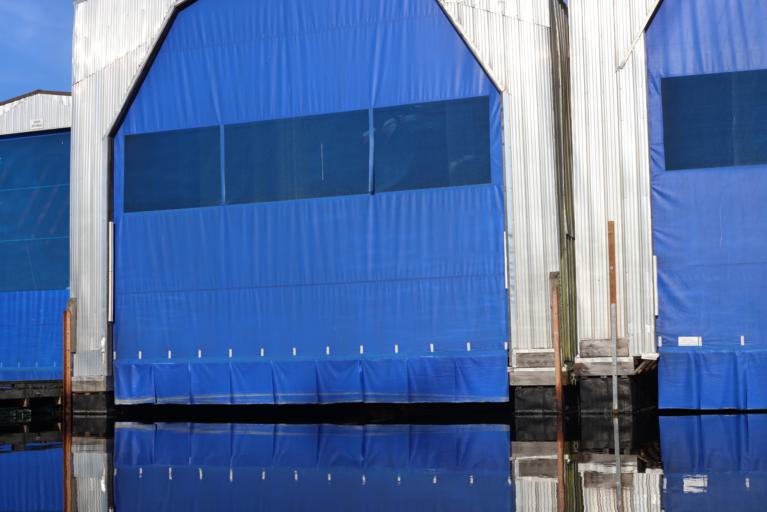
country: CA
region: British Columbia
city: North Saanich
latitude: 48.6780
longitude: -123.4137
